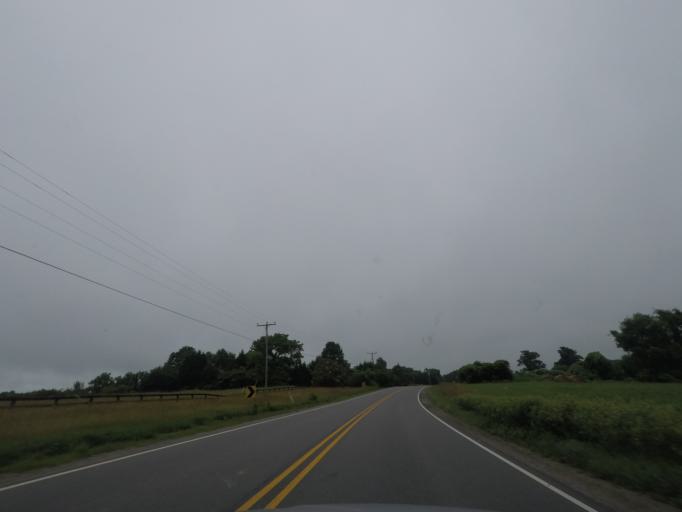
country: US
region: Virginia
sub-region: Fluvanna County
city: Weber City
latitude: 37.6184
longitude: -78.3765
